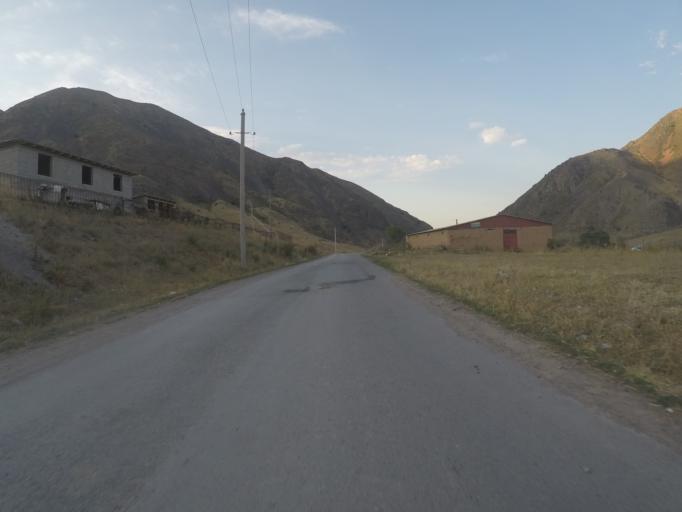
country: KG
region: Chuy
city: Bishkek
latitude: 42.6761
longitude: 74.6536
